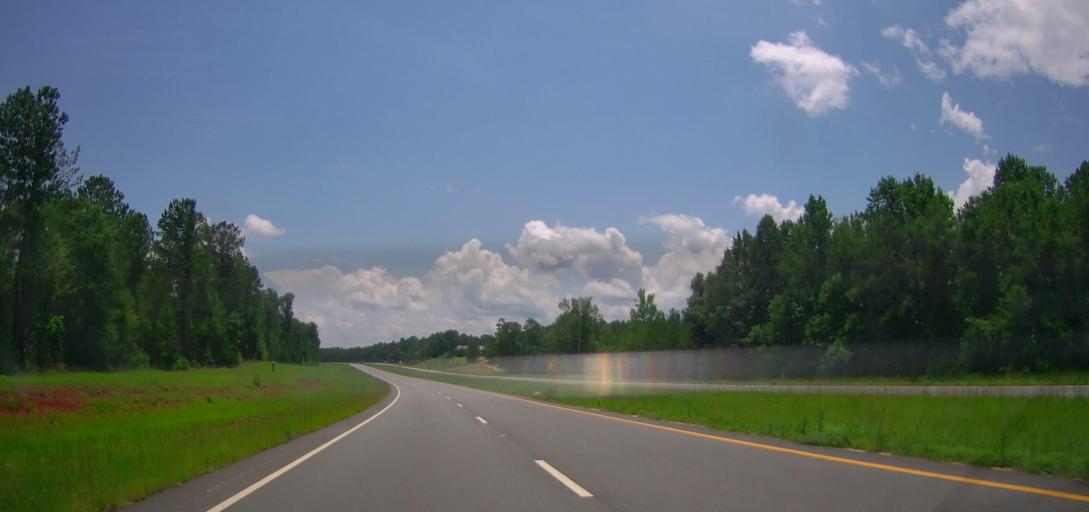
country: US
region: Georgia
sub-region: Upson County
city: Thomaston
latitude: 32.8139
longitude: -84.2867
